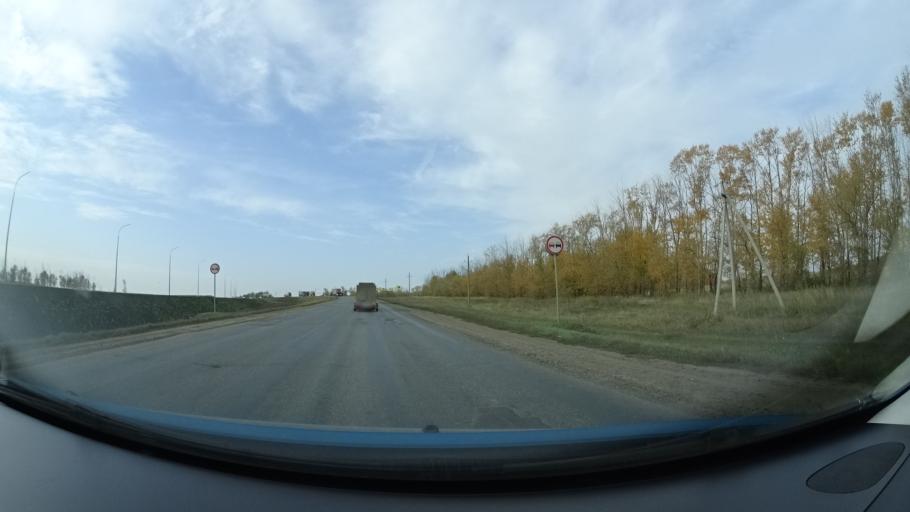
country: RU
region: Bashkortostan
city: Buzdyak
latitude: 54.6392
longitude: 54.4857
